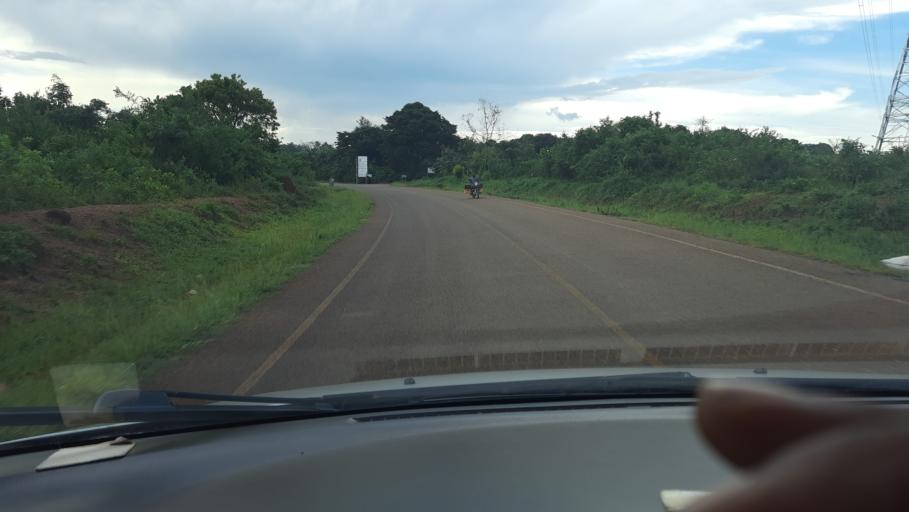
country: UG
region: Central Region
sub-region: Nakasongola District
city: Nakasongola
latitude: 1.3253
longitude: 32.4275
